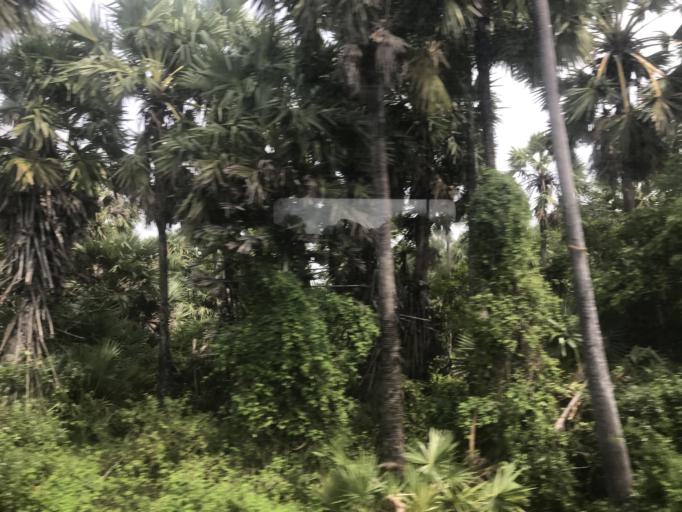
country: LK
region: Northern Province
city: Kilinochchi
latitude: 9.5963
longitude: 80.3423
